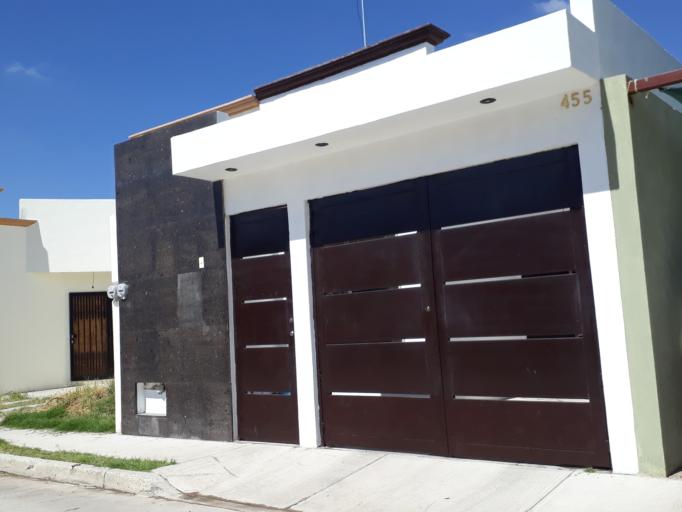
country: MX
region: Aguascalientes
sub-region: Aguascalientes
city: San Sebastian [Fraccionamiento]
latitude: 21.8376
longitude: -102.3007
